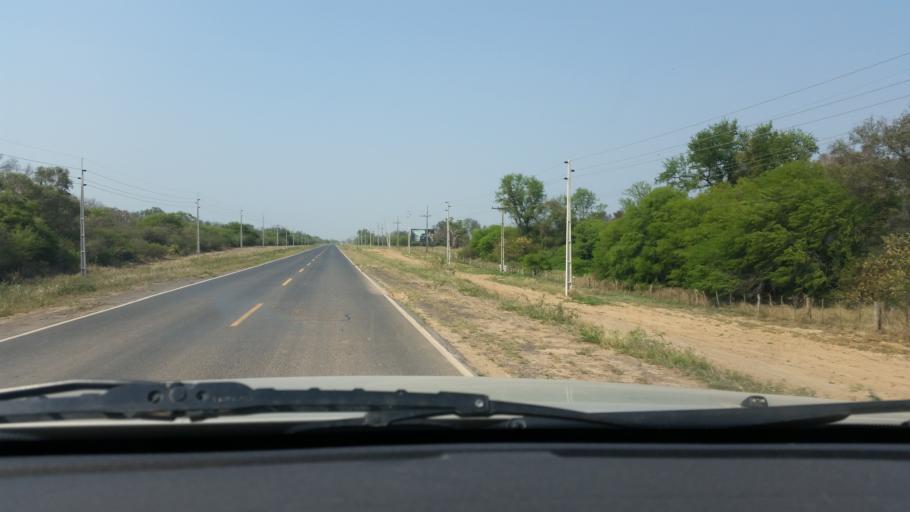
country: PY
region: Boqueron
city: Filadelfia
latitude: -22.3977
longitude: -60.0350
